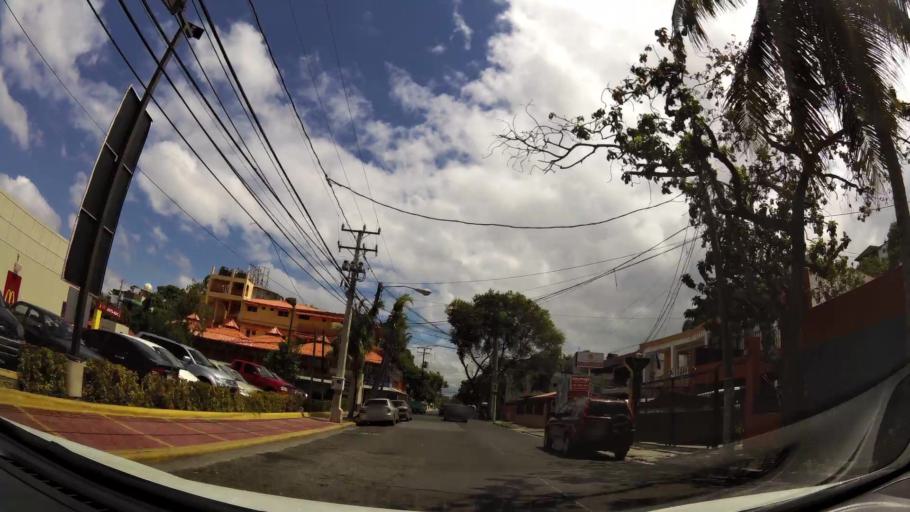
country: DO
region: Nacional
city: Bella Vista
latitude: 18.4574
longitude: -69.9555
